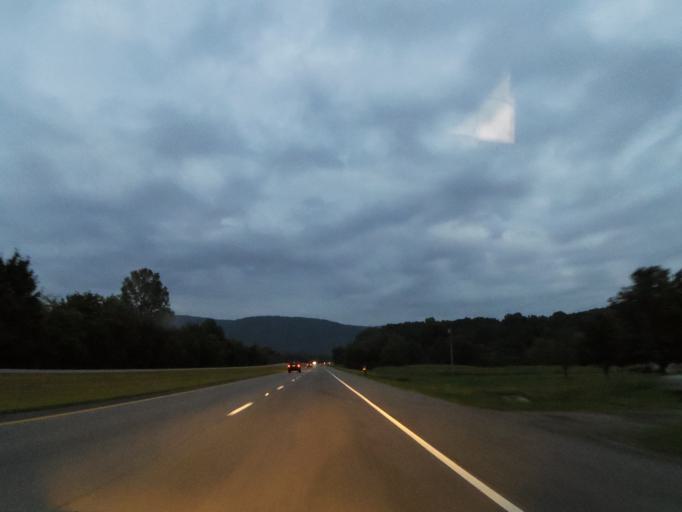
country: US
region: Alabama
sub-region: Madison County
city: Owens Cross Roads
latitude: 34.6834
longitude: -86.3366
